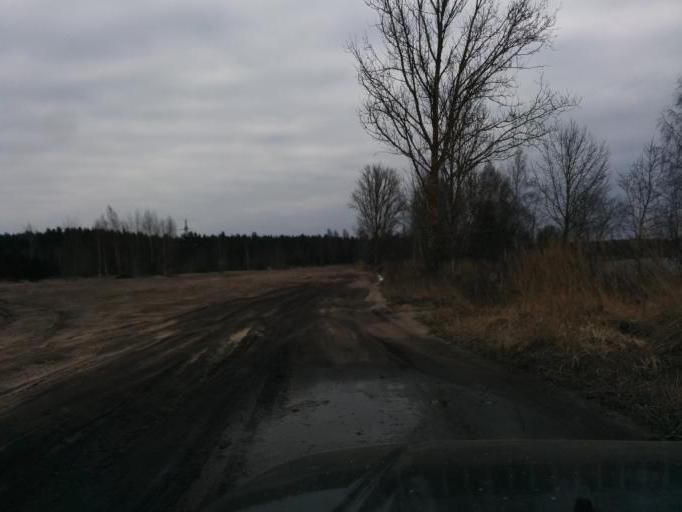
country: LV
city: Tireli
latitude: 56.9409
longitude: 23.6420
